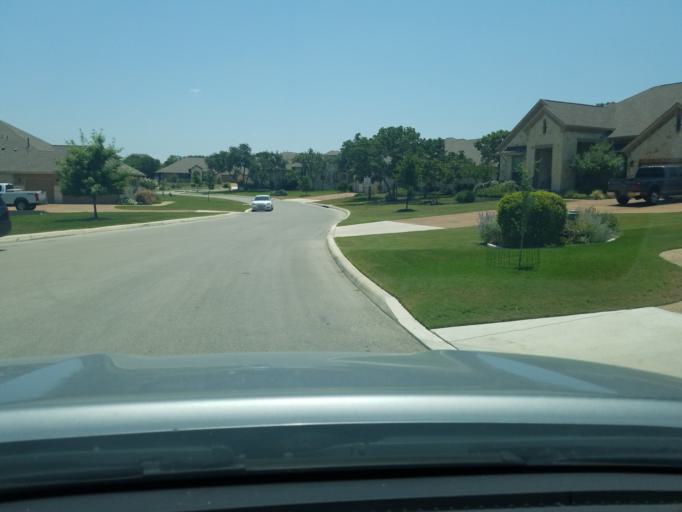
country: US
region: Texas
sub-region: Bexar County
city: Timberwood Park
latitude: 29.7115
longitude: -98.5123
